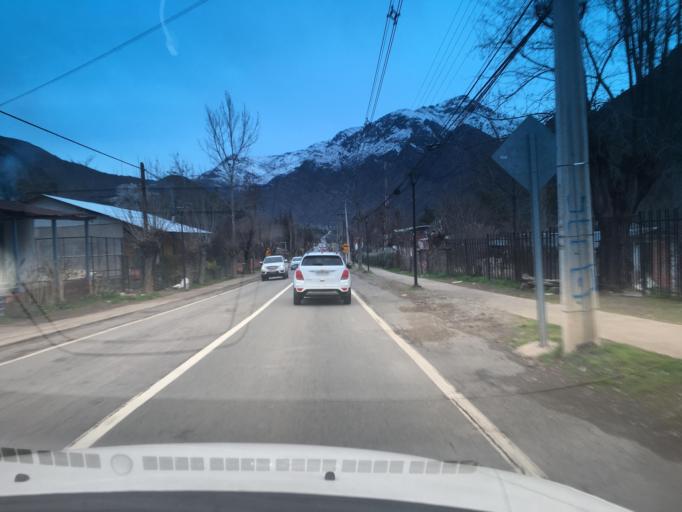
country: CL
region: Santiago Metropolitan
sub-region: Provincia de Cordillera
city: Puente Alto
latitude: -33.6924
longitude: -70.3355
